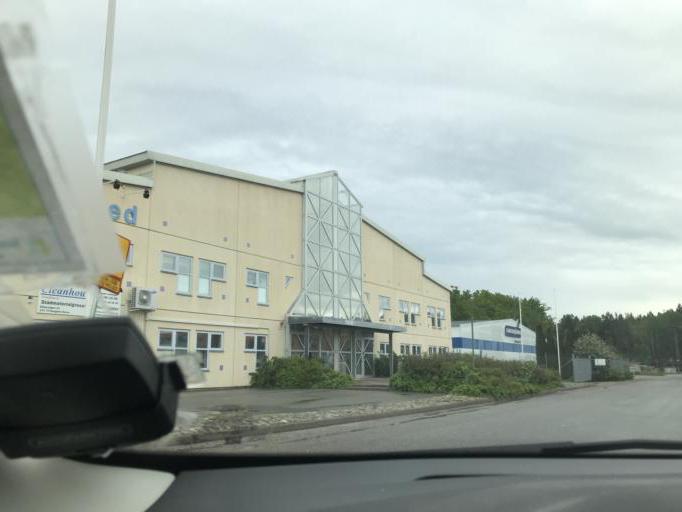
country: SE
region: Stockholm
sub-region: Huddinge Kommun
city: Segeltorp
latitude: 59.2676
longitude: 17.9274
